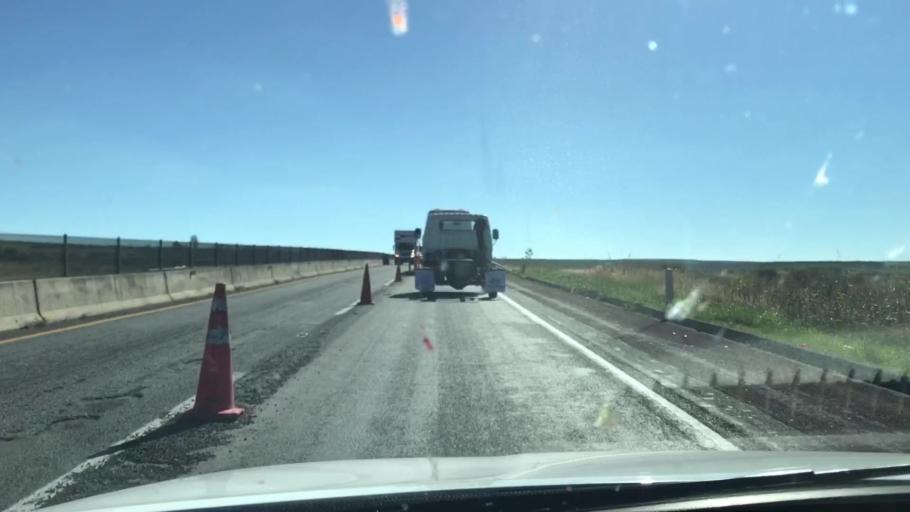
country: MX
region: Jalisco
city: Jalostotitlan
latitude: 21.1032
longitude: -102.4729
